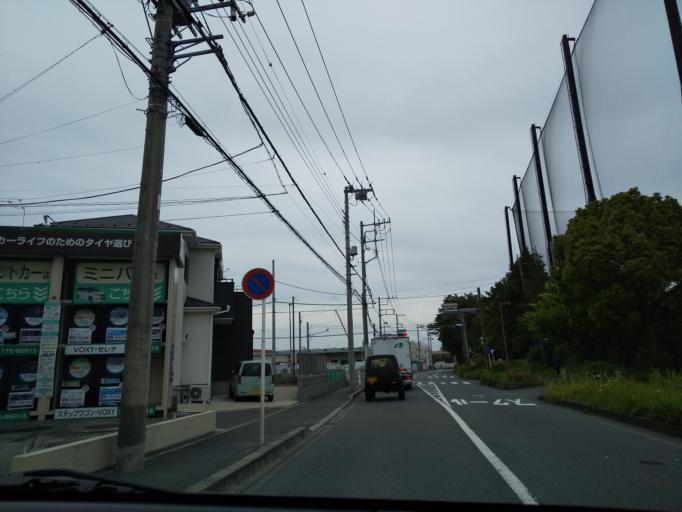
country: JP
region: Tokyo
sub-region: Machida-shi
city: Machida
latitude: 35.5499
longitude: 139.4004
